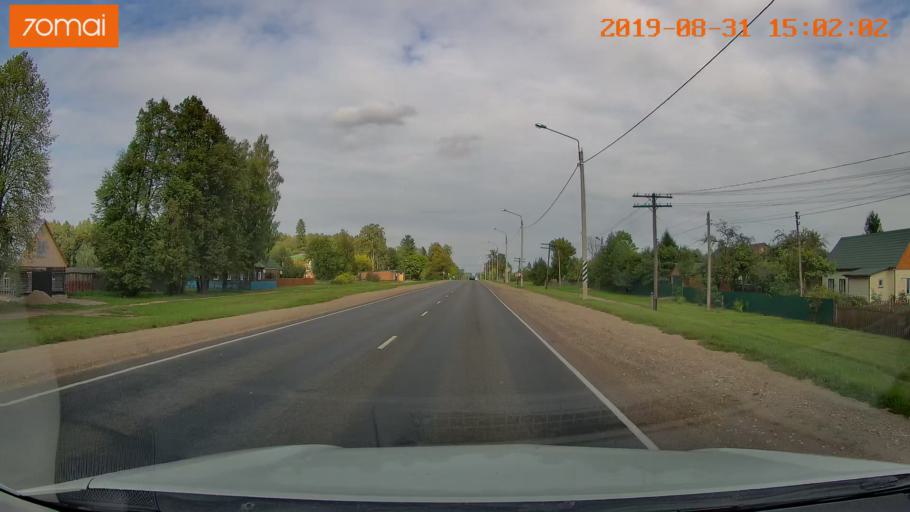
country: RU
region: Kaluga
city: Spas-Demensk
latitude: 54.3430
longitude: 34.0678
